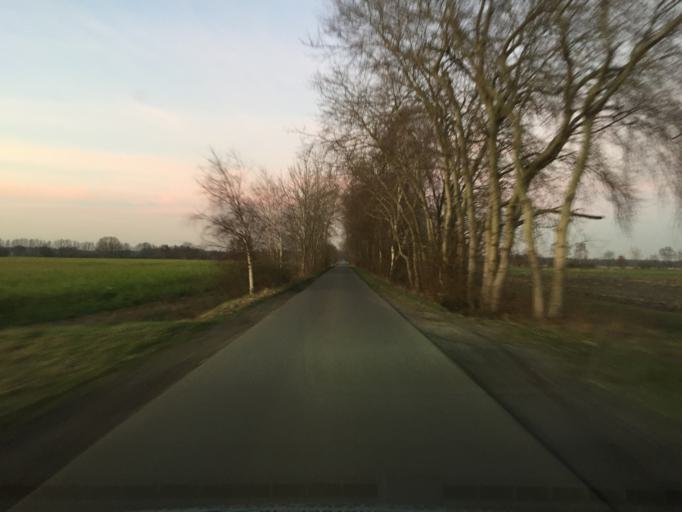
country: DE
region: Lower Saxony
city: Sulingen
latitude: 52.6503
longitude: 8.8339
